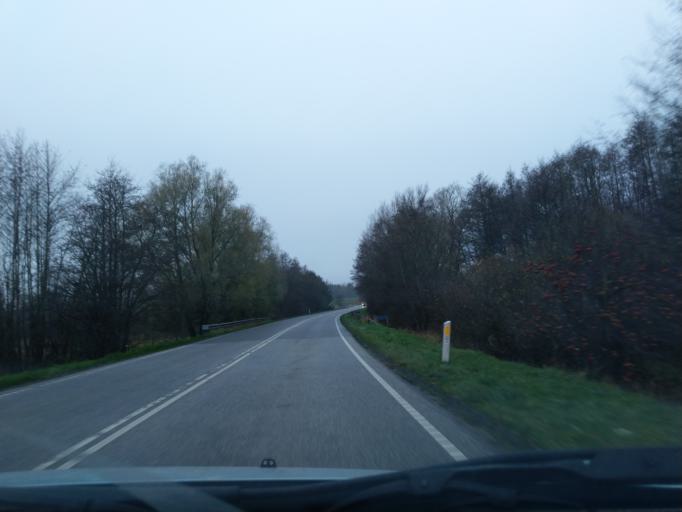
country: DK
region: Zealand
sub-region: Vordingborg Kommune
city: Praesto
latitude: 55.1132
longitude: 12.0354
